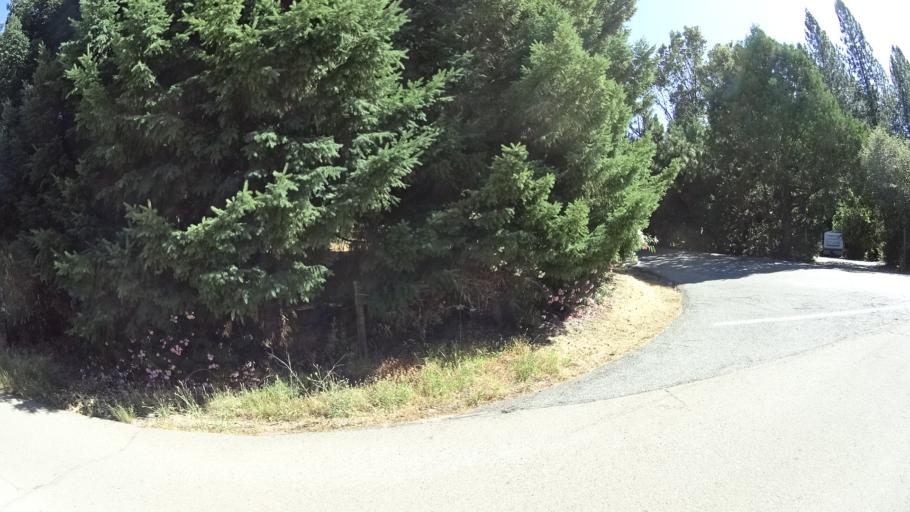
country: US
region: California
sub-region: Amador County
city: Pioneer
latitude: 38.4012
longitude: -120.5061
